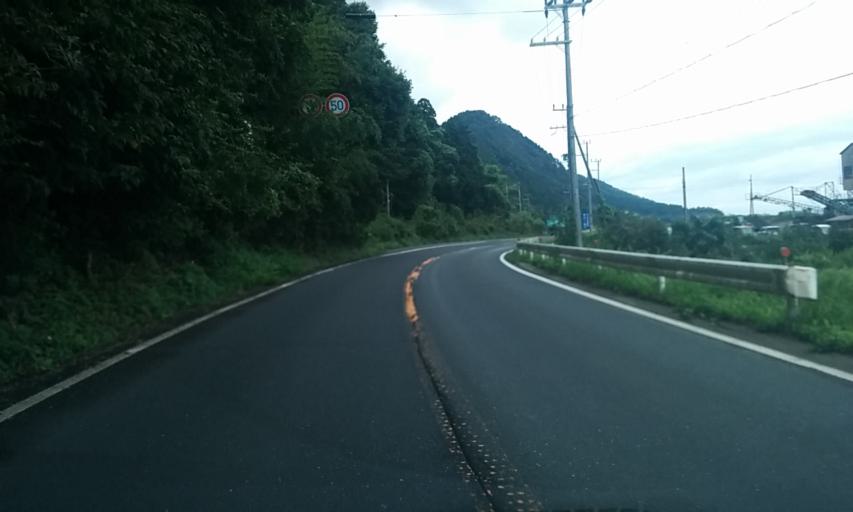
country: JP
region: Kyoto
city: Maizuru
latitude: 35.4797
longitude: 135.2779
